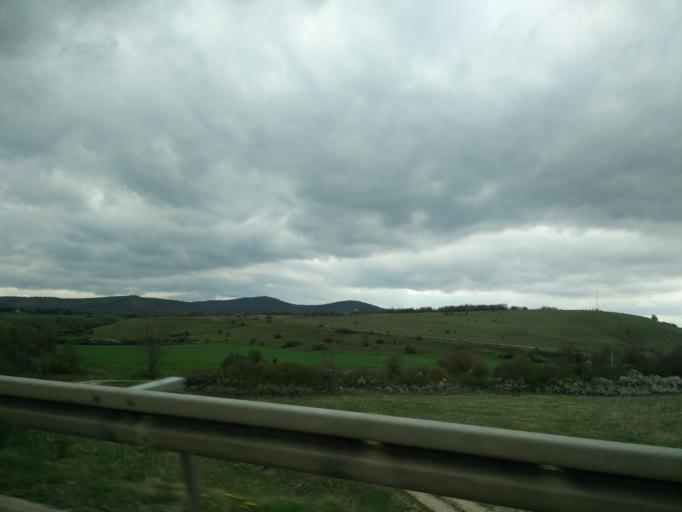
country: HR
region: Zadarska
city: Gracac
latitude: 44.5369
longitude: 15.7511
